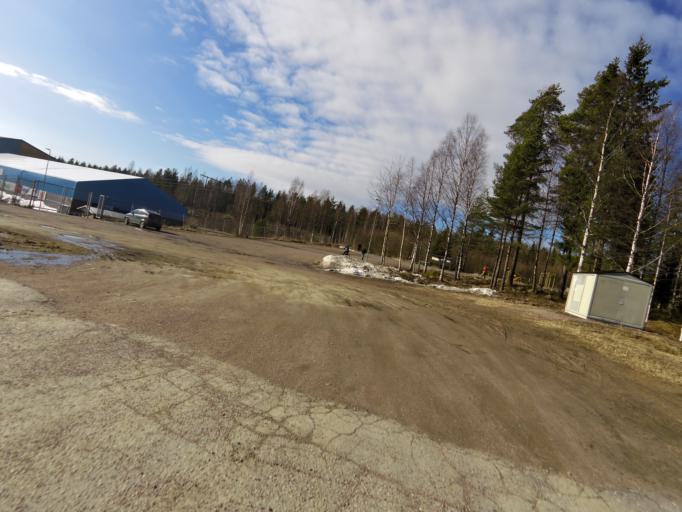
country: SE
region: Gaevleborg
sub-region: Hofors Kommun
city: Hofors
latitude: 60.5455
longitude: 16.2682
